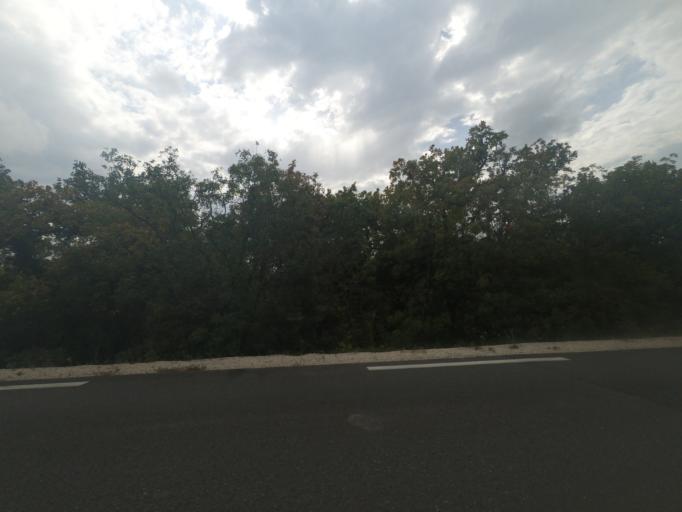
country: FR
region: Languedoc-Roussillon
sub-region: Departement de l'Herault
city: Les Matelles
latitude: 43.7432
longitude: 3.7679
